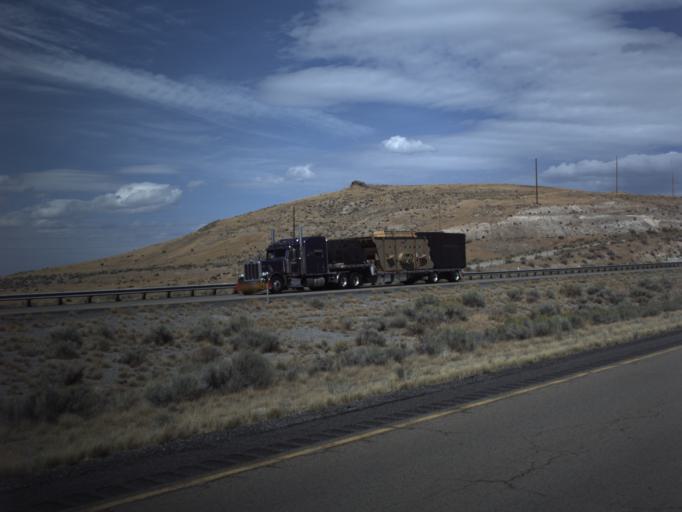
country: US
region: Utah
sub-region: Tooele County
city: Grantsville
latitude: 40.8167
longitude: -112.9150
